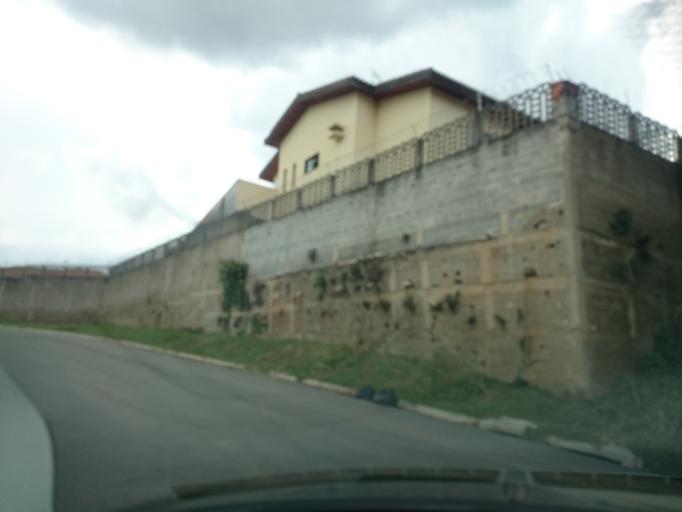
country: BR
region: Sao Paulo
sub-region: Sorocaba
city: Sorocaba
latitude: -23.4755
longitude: -47.4041
